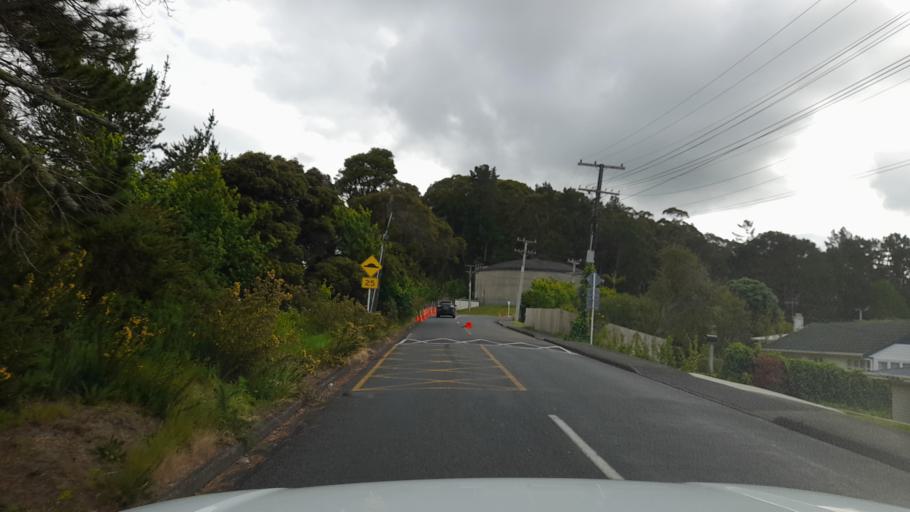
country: NZ
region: Northland
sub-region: Whangarei
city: Whangarei
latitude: -35.7396
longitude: 174.3173
